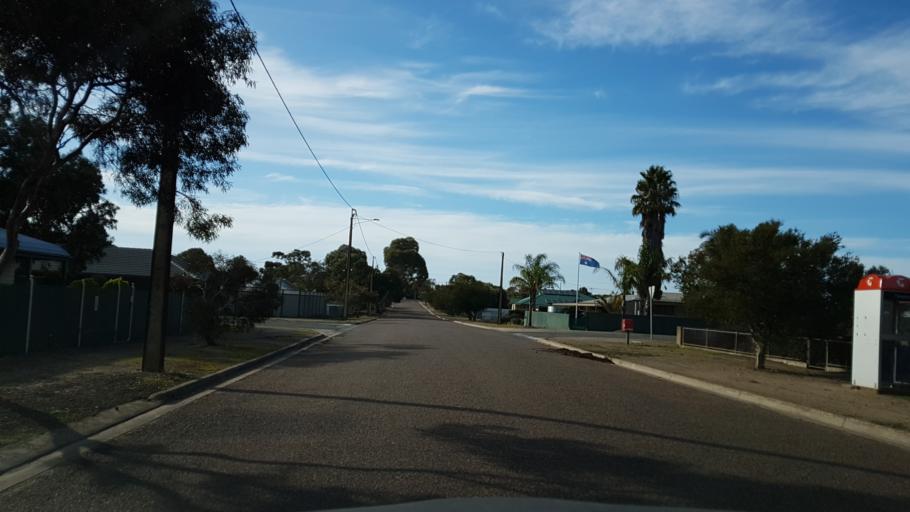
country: AU
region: South Australia
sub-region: Murray Bridge
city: Tailem Bend
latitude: -35.2527
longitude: 139.4589
